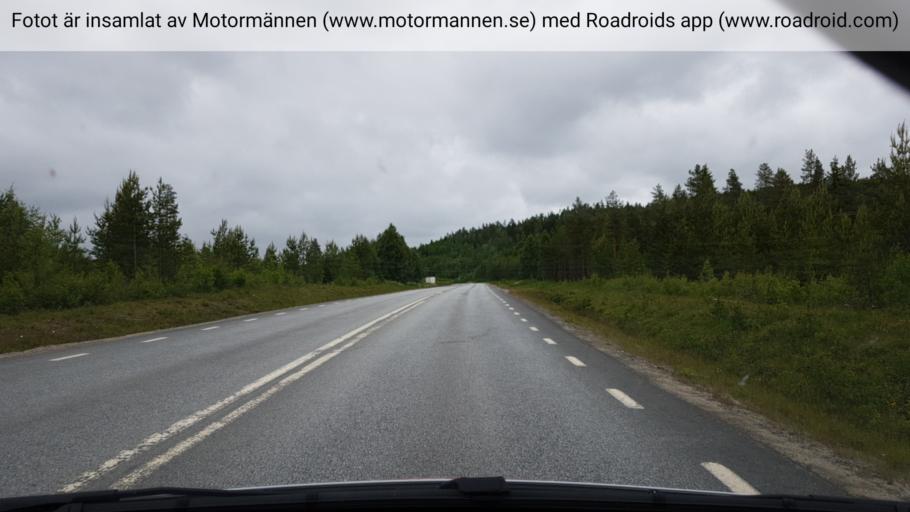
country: SE
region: Vaesterbotten
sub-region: Vannas Kommun
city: Vaennaes
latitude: 63.9859
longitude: 19.7294
